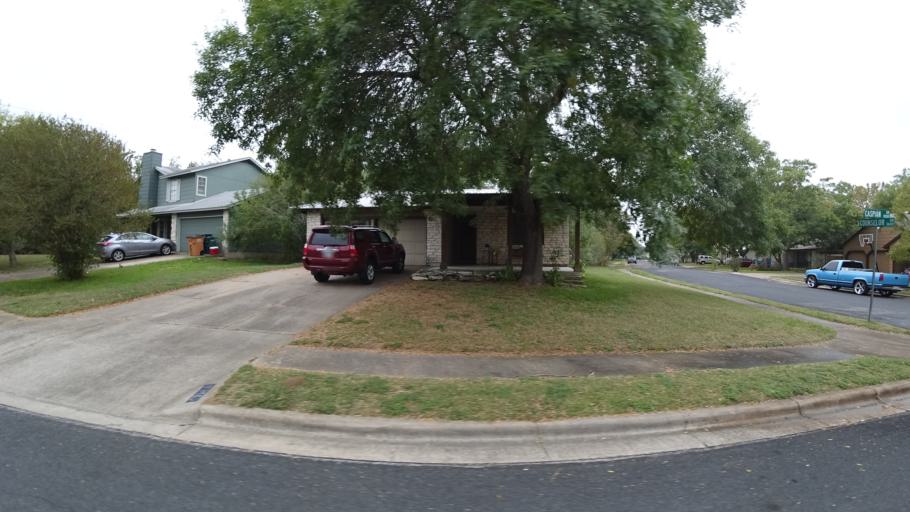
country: US
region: Texas
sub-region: Travis County
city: Shady Hollow
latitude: 30.2000
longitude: -97.8413
